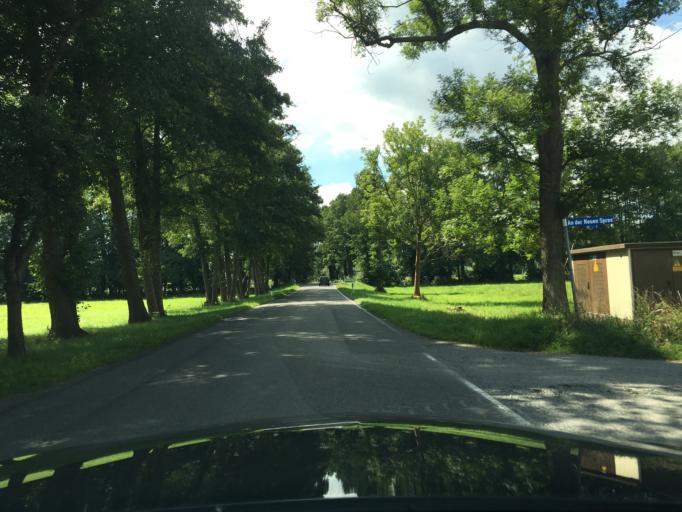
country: DE
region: Brandenburg
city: Burg
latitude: 51.8525
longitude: 14.1052
